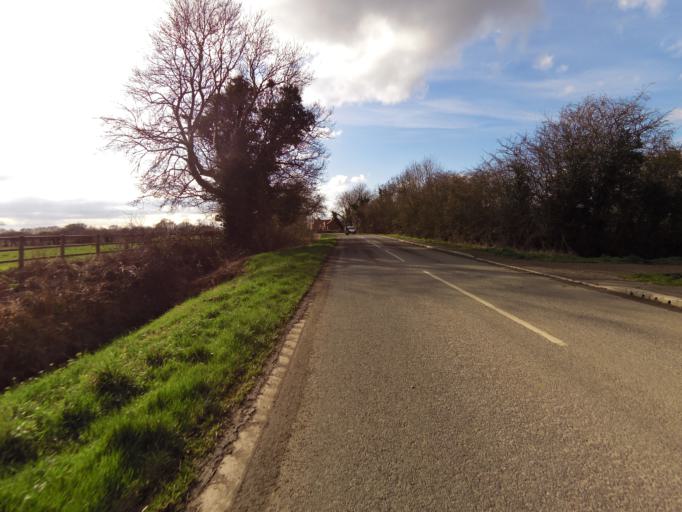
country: GB
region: England
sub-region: East Riding of Yorkshire
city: Pollington
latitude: 53.6477
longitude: -1.0409
